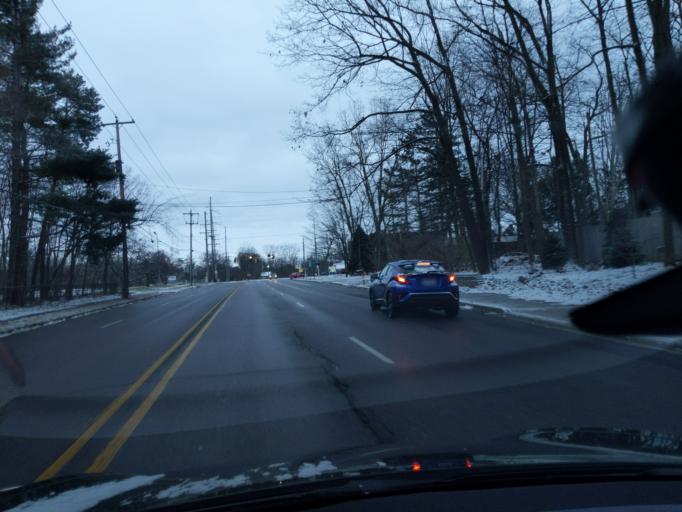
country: US
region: Michigan
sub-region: Ingham County
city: Okemos
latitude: 42.7119
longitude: -84.4330
